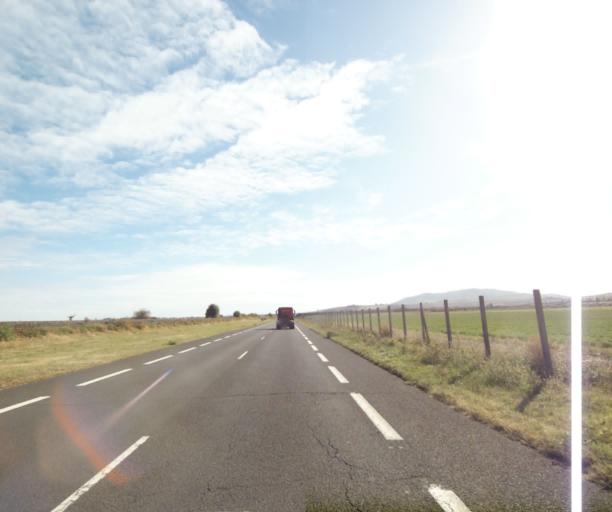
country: FR
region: Auvergne
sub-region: Departement du Puy-de-Dome
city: Malintrat
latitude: 45.7905
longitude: 3.1914
